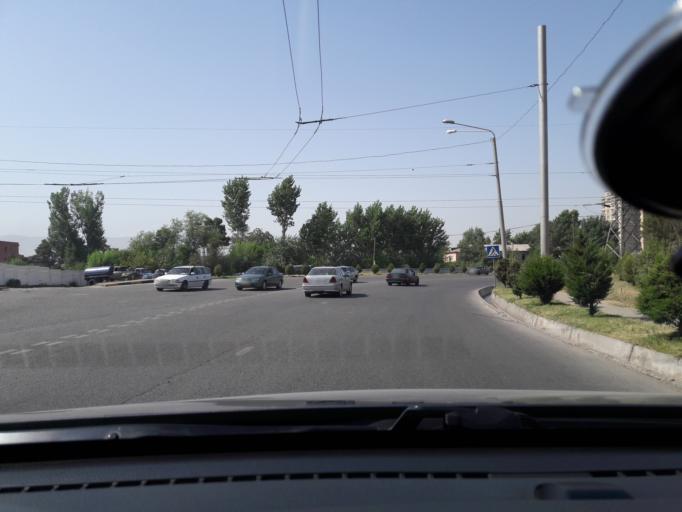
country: TJ
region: Dushanbe
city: Dushanbe
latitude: 38.5040
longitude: 68.7617
